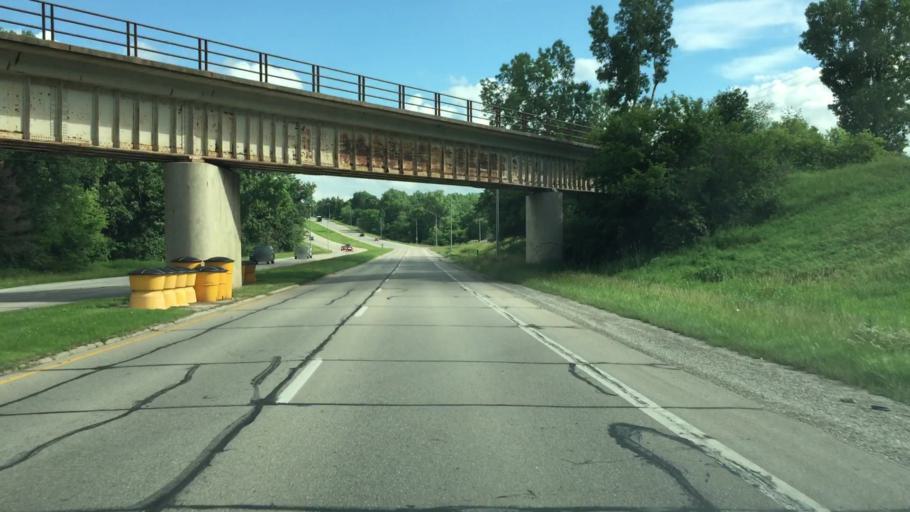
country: US
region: Iowa
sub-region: Jasper County
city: Newton
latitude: 41.6952
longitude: -93.0768
